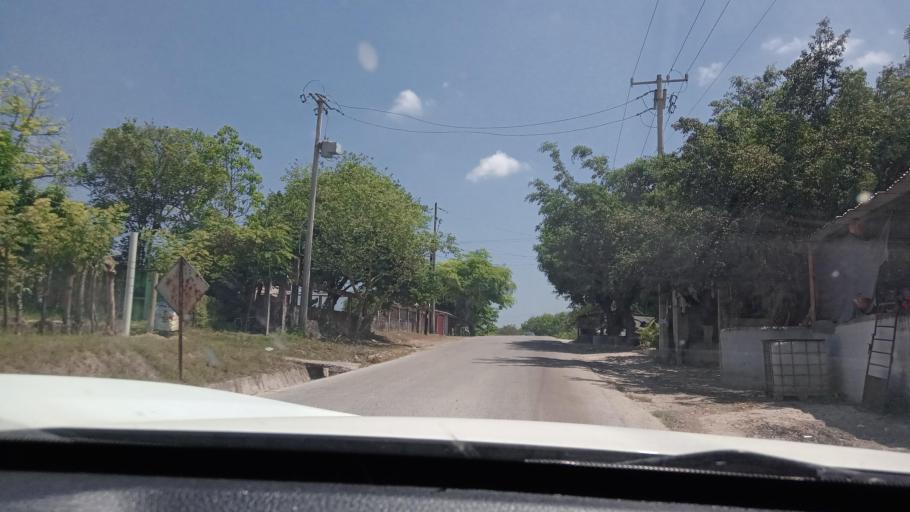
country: MX
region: Veracruz
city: Las Choapas
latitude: 17.7542
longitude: -94.1127
